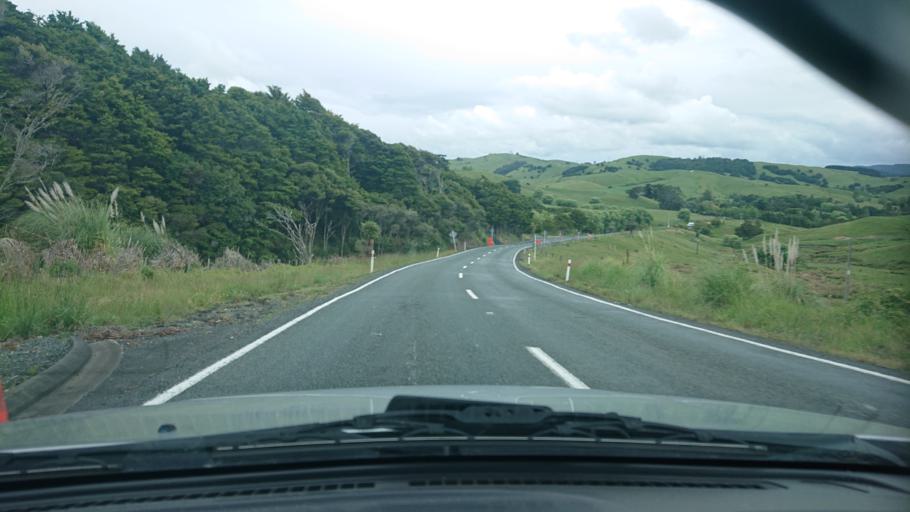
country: NZ
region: Auckland
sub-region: Auckland
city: Wellsford
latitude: -36.3695
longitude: 174.4530
